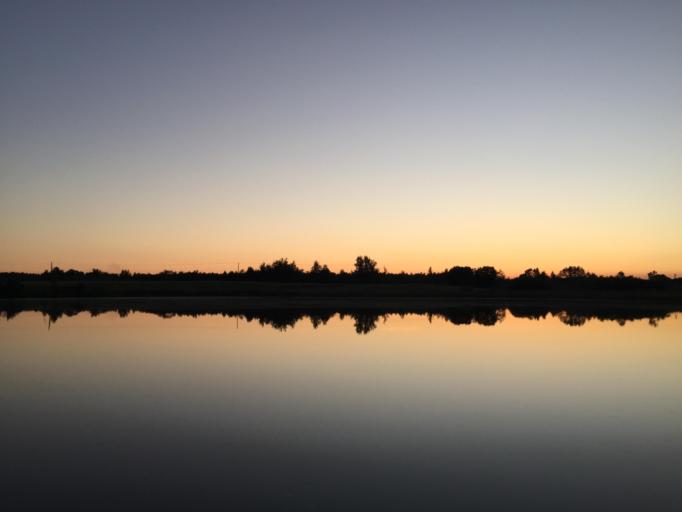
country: LV
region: Rezekne
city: Rezekne
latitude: 56.3696
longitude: 27.4123
